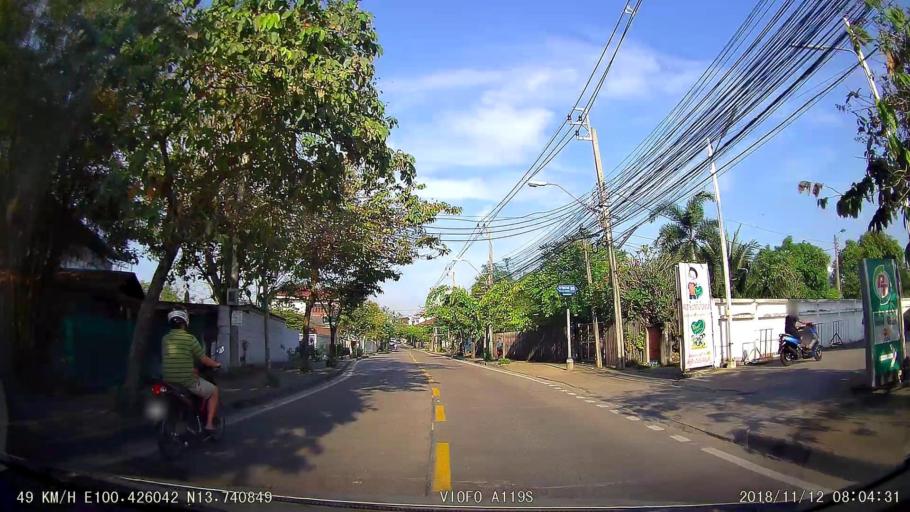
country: TH
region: Bangkok
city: Phasi Charoen
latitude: 13.7409
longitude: 100.4259
